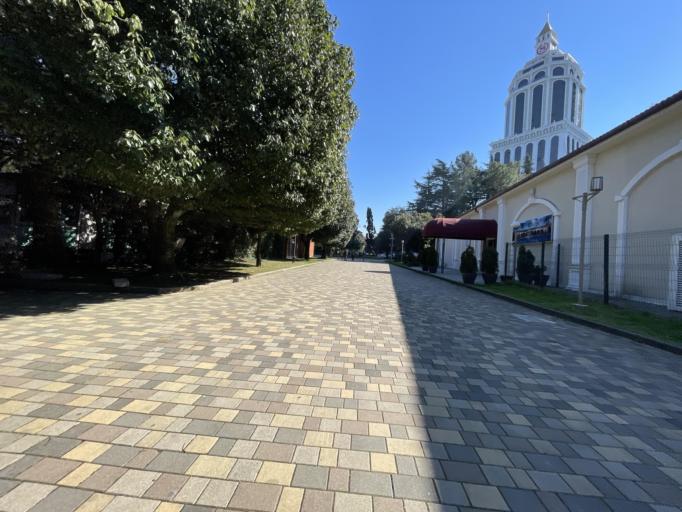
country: GE
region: Ajaria
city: Batumi
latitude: 41.6523
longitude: 41.6301
